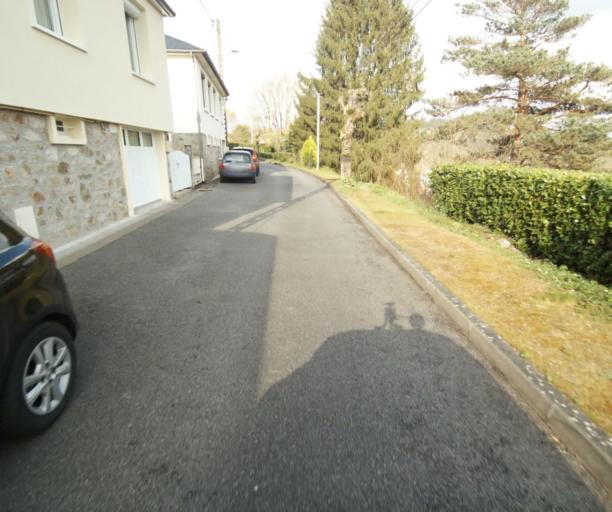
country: FR
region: Limousin
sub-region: Departement de la Correze
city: Tulle
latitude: 45.2534
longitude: 1.7527
